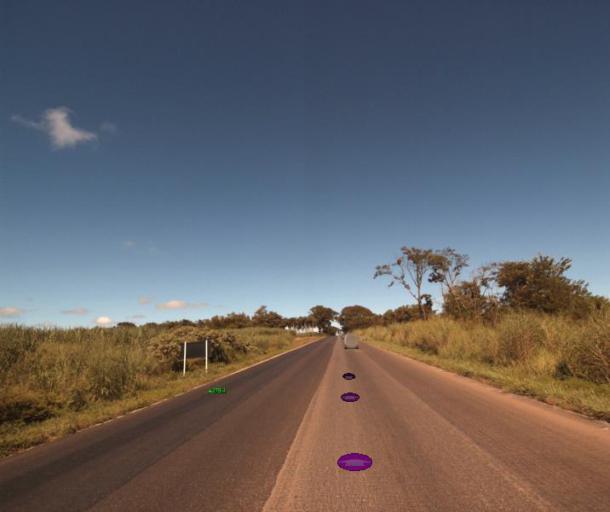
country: BR
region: Goias
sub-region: Itapaci
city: Itapaci
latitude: -15.1285
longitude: -49.5105
